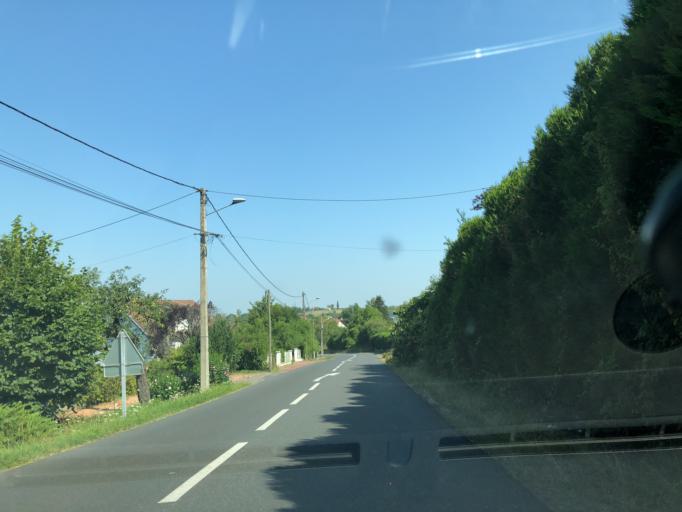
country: FR
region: Auvergne
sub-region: Departement de l'Allier
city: Cusset
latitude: 46.1299
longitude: 3.4757
